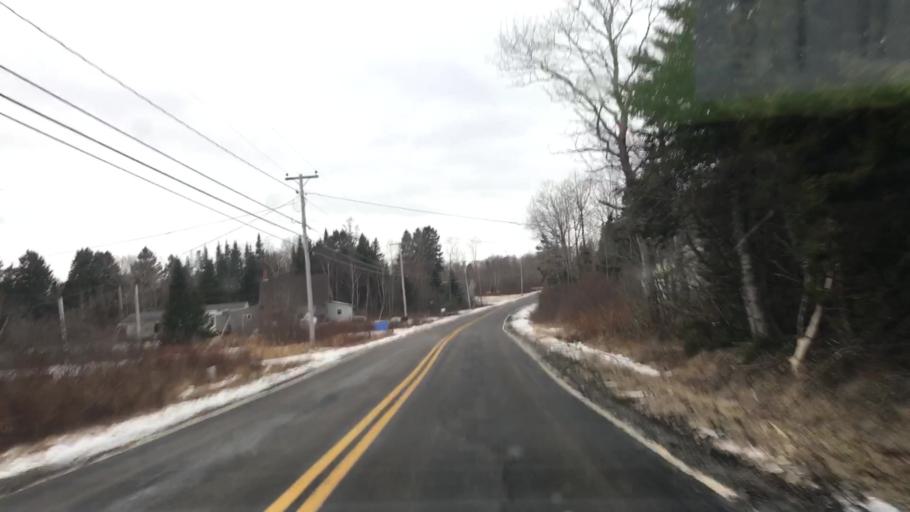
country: US
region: Maine
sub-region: Washington County
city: Machiasport
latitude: 44.7017
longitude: -67.3436
